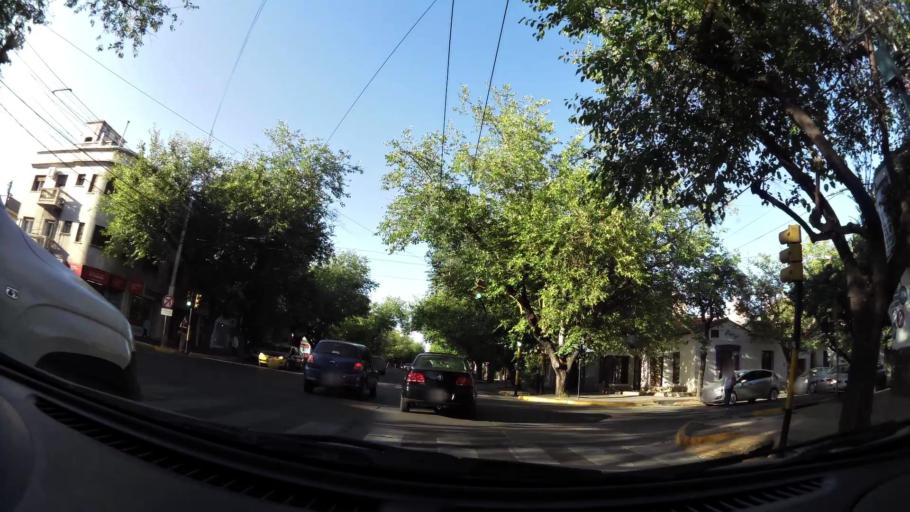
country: AR
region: Mendoza
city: Mendoza
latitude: -32.9070
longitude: -68.8438
